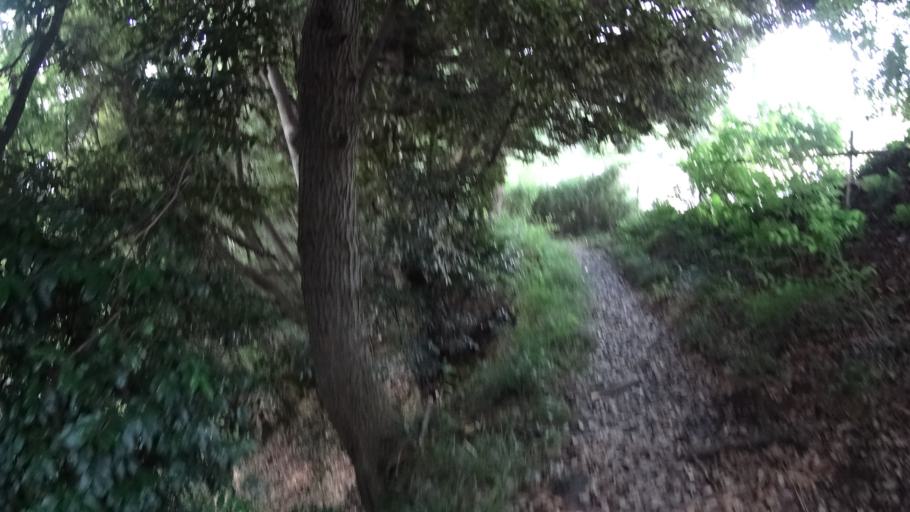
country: JP
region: Kanagawa
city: Zushi
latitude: 35.3034
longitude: 139.6197
